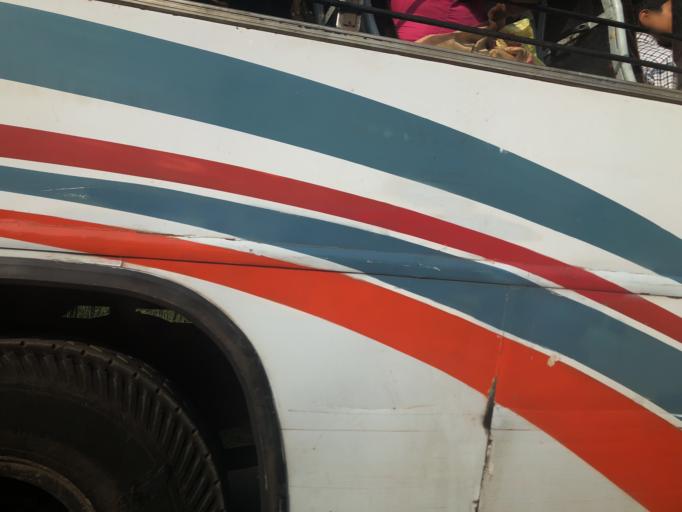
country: IN
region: Karnataka
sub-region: Dakshina Kannada
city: Ullal
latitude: 12.8155
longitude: 74.8517
